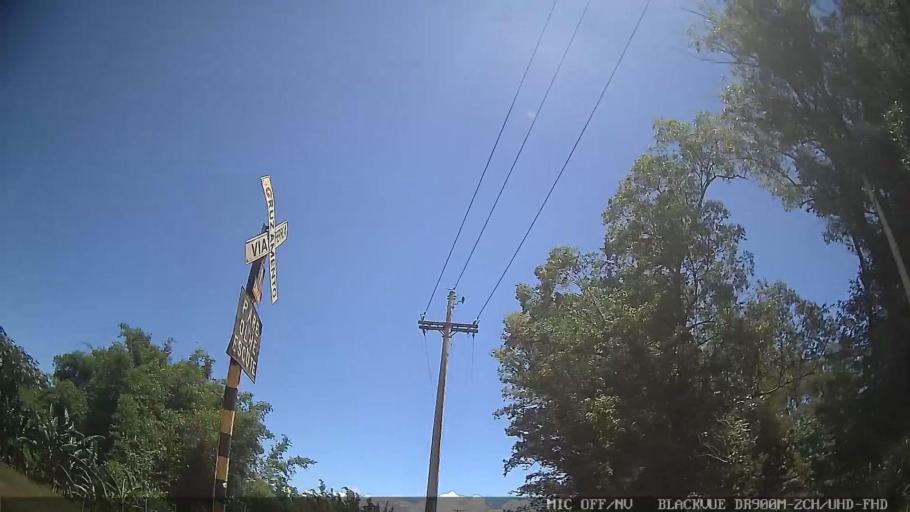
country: BR
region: Sao Paulo
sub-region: Jaguariuna
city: Jaguariuna
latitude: -22.7179
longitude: -46.9886
